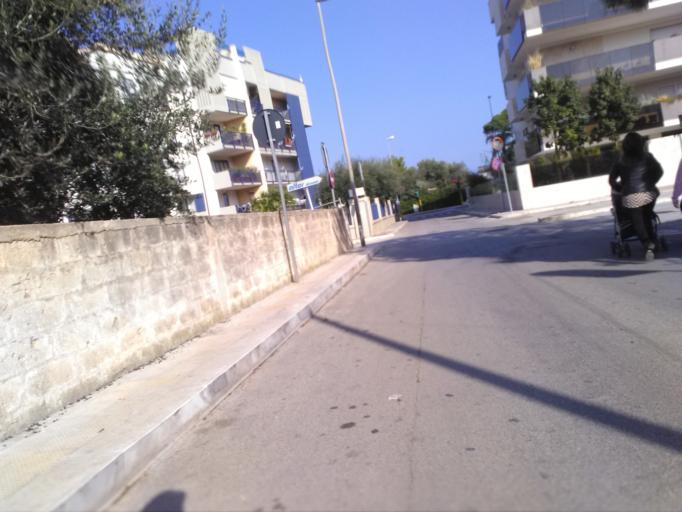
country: IT
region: Apulia
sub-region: Provincia di Bari
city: San Paolo
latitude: 41.1551
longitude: 16.7686
